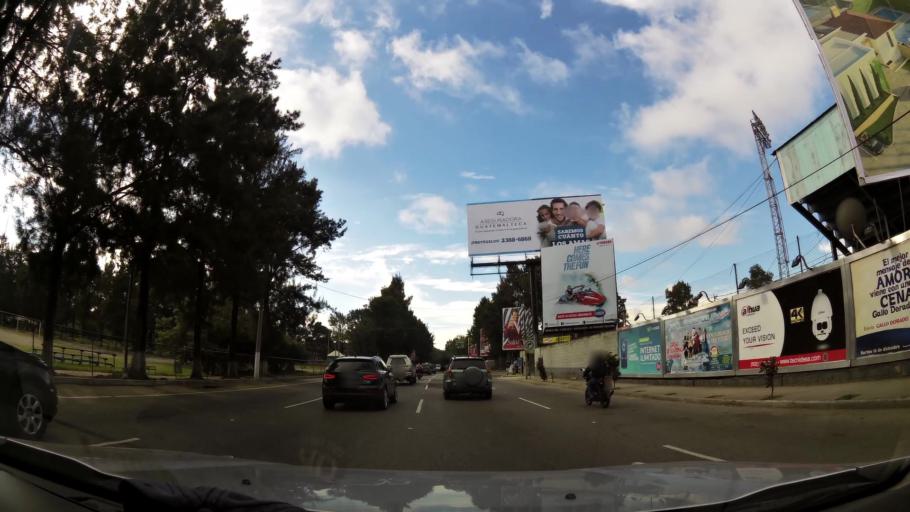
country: GT
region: Guatemala
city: Guatemala City
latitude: 14.6150
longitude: -90.5091
